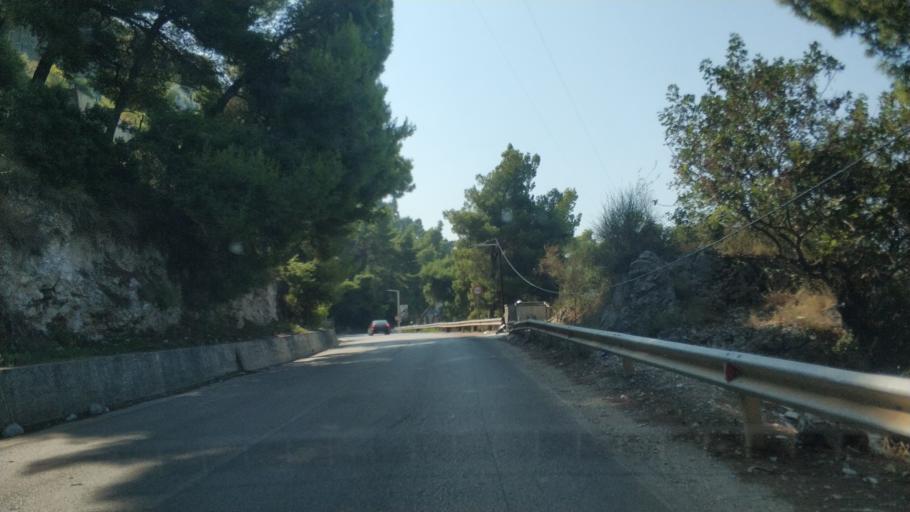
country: AL
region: Vlore
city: Vlore
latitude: 40.4077
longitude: 19.4807
